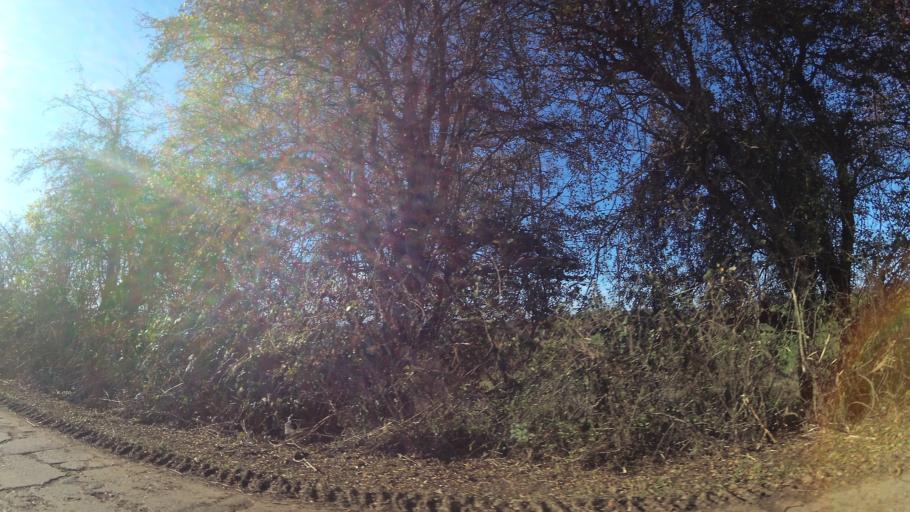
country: DE
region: Saarland
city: Losheim
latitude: 49.4762
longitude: 6.7429
